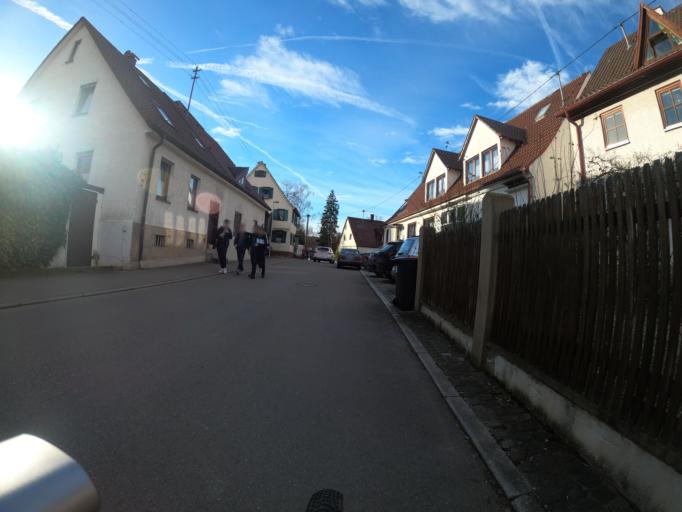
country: DE
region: Baden-Wuerttemberg
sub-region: Regierungsbezirk Stuttgart
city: Kirchheim unter Teck
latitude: 48.6508
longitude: 9.4560
